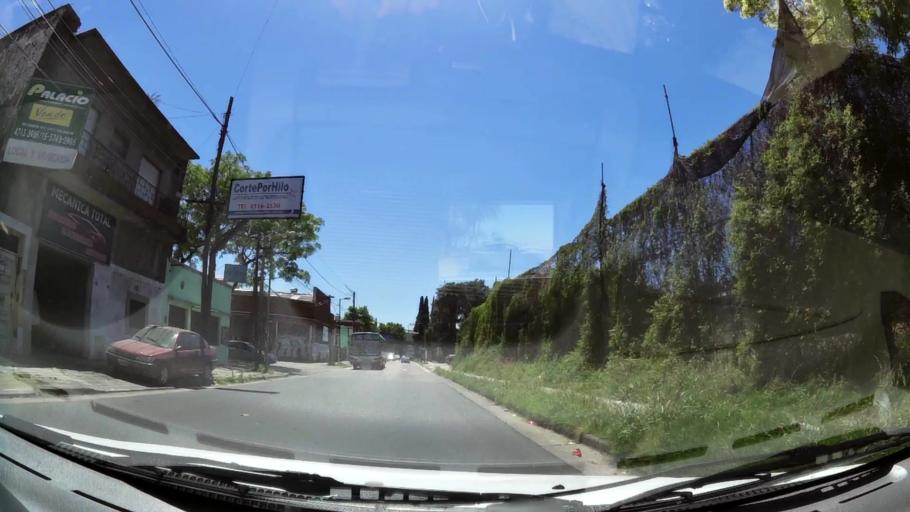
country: AR
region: Buenos Aires
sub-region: Partido de General San Martin
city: General San Martin
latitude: -34.5563
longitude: -58.5338
